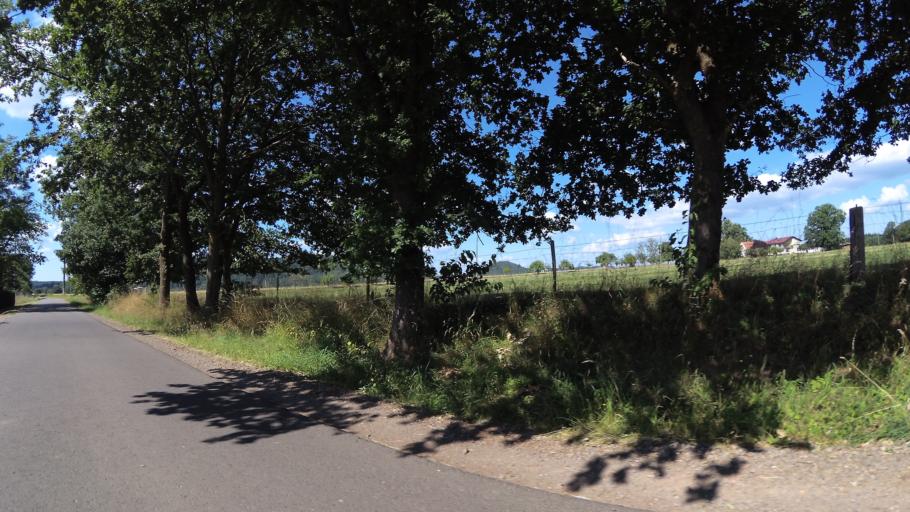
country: DE
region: Saarland
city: Weiskirchen
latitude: 49.5027
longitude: 6.8204
